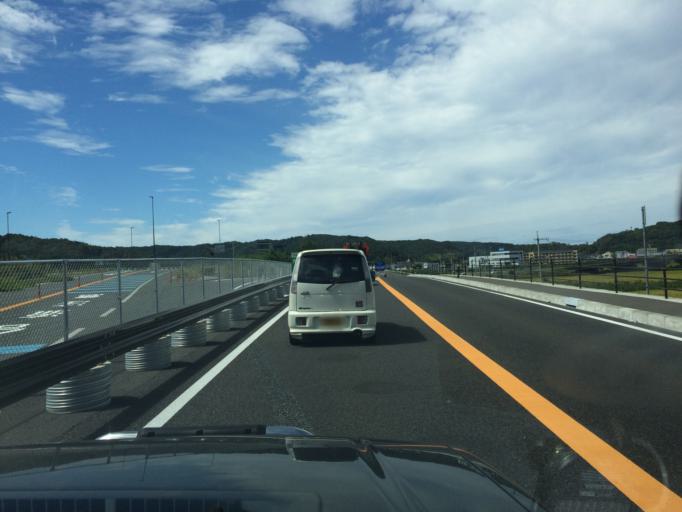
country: JP
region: Tottori
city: Kurayoshi
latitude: 35.5124
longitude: 134.0048
